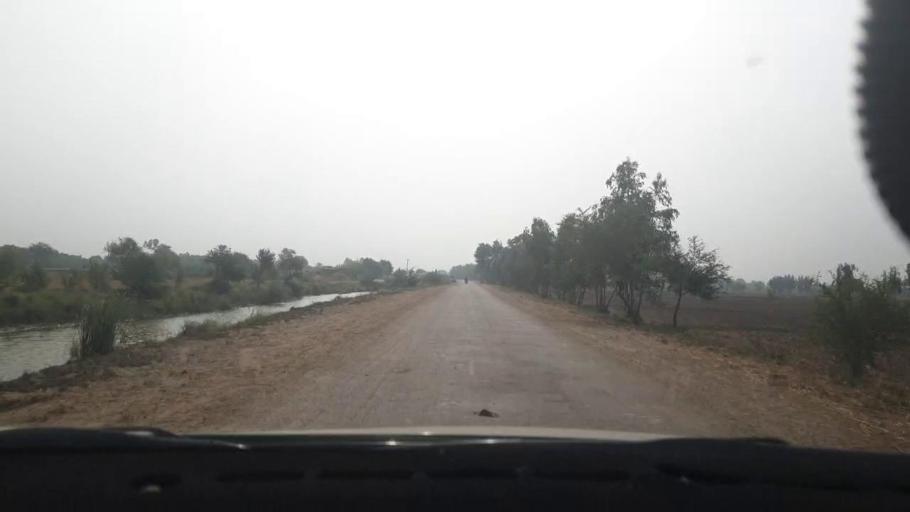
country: PK
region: Sindh
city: Tando Muhammad Khan
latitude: 25.0519
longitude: 68.5503
